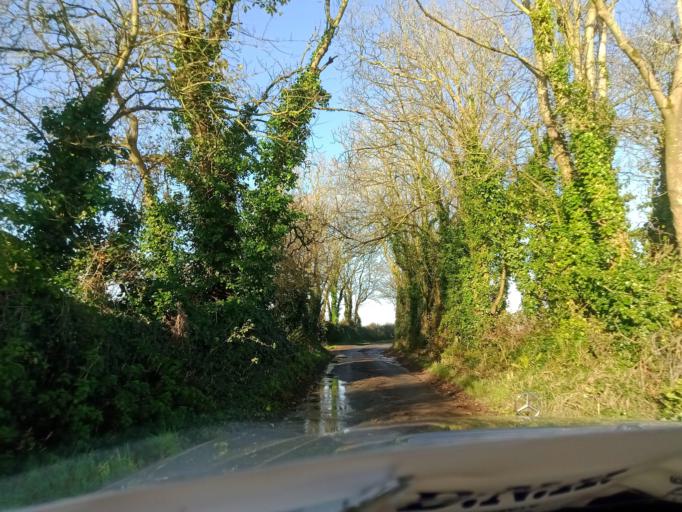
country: IE
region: Munster
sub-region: Waterford
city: Waterford
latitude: 52.2881
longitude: -7.1707
